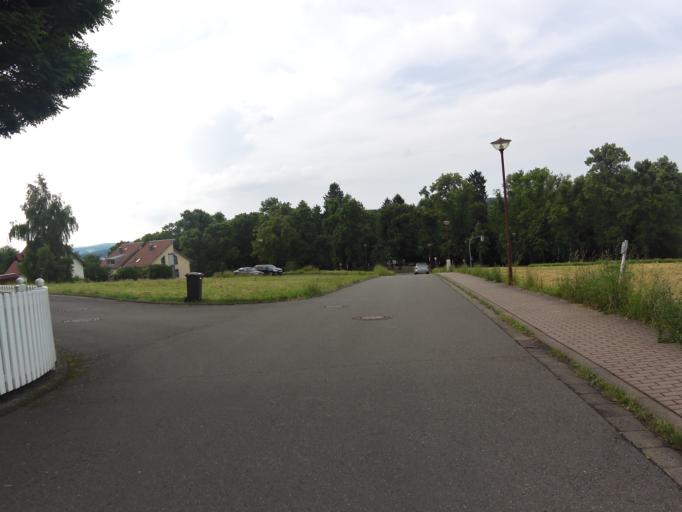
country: DE
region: Thuringia
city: Bad Salzungen
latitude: 50.8061
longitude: 10.2356
